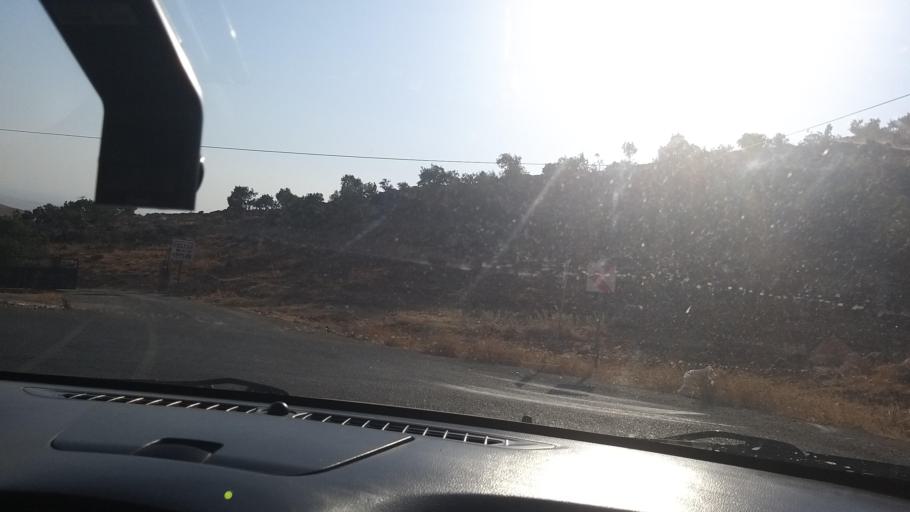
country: TR
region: Diyarbakir
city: Silvan
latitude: 38.1930
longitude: 41.0066
